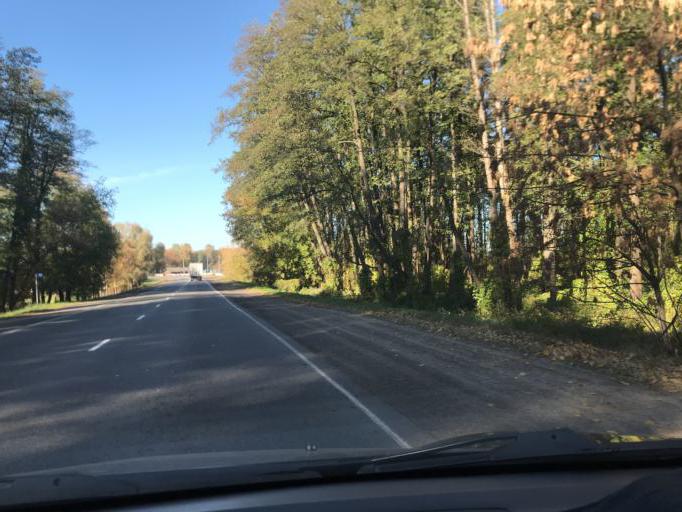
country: BY
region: Gomel
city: Kalinkavichy
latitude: 52.3771
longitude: 29.3513
